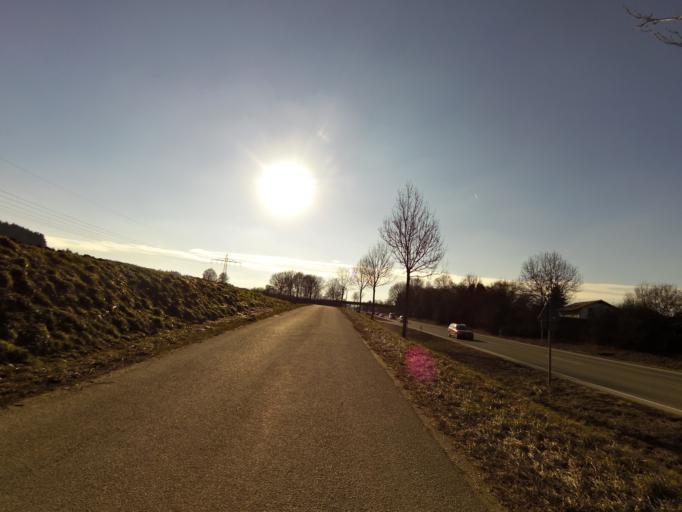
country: DE
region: Bavaria
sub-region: Lower Bavaria
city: Eching
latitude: 48.5088
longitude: 12.0814
